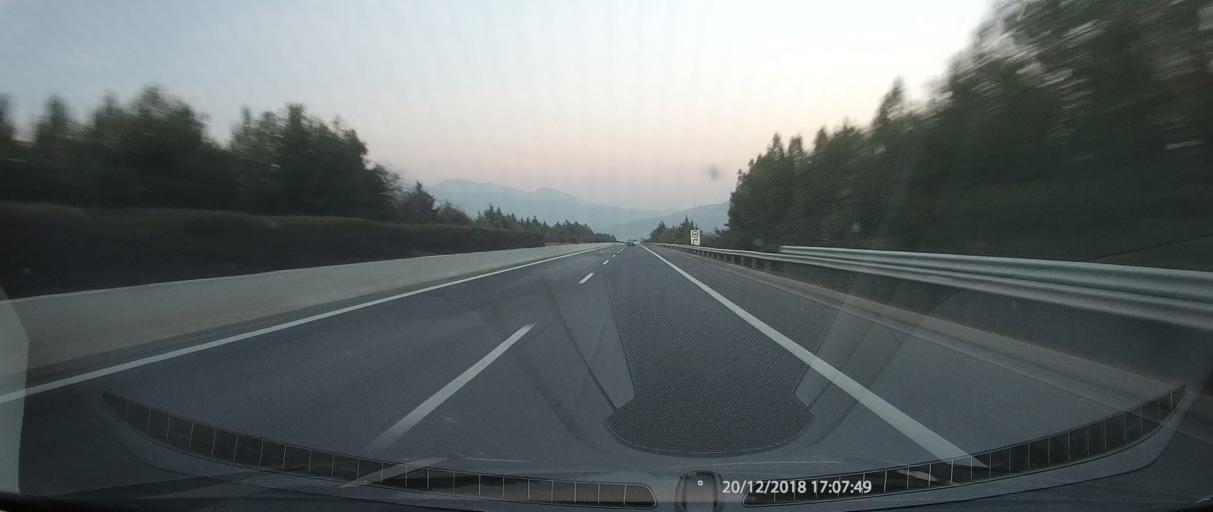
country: GR
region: Thessaly
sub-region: Nomos Larisis
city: Makrychori
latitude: 39.7858
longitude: 22.4926
